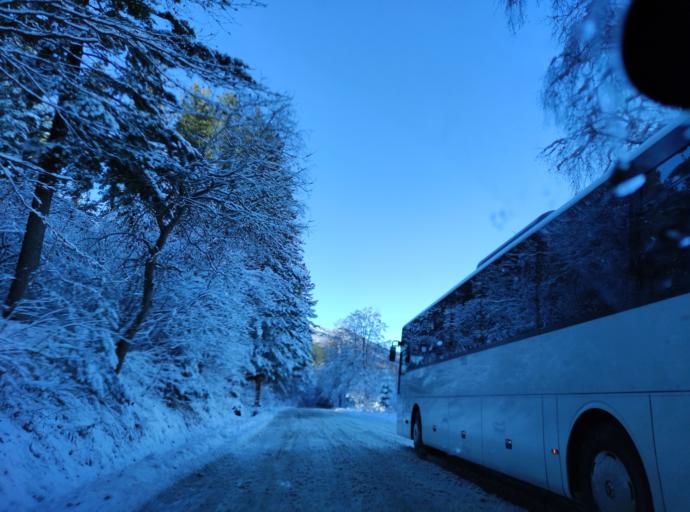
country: BG
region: Sofia-Capital
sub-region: Stolichna Obshtina
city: Sofia
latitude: 42.5945
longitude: 23.3114
